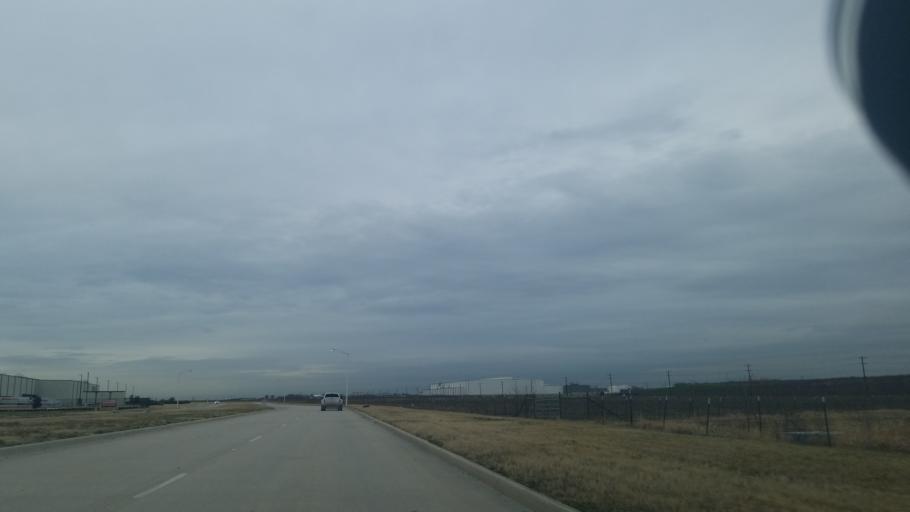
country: US
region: Texas
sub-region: Denton County
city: Denton
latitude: 33.2086
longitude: -97.1848
